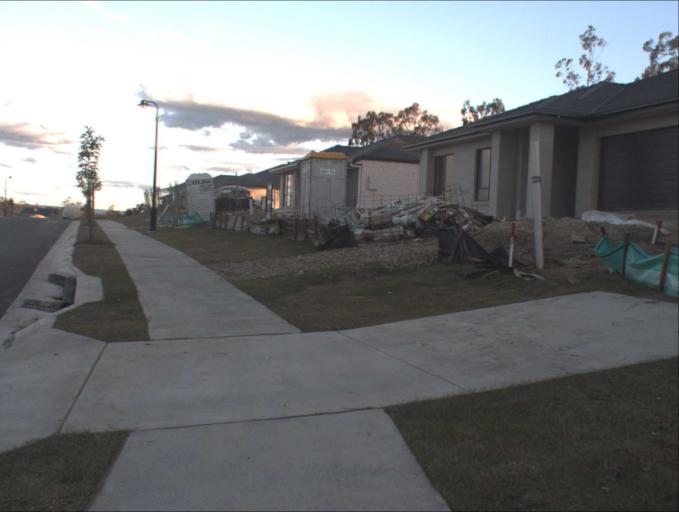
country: AU
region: Queensland
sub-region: Logan
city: North Maclean
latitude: -27.7988
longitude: 152.9527
